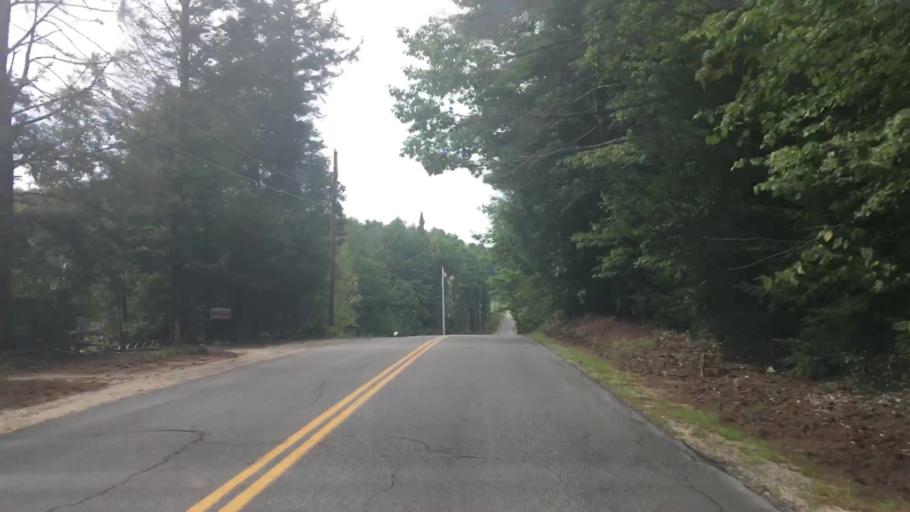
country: US
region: Maine
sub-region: Oxford County
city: Oxford
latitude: 44.0590
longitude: -70.5605
